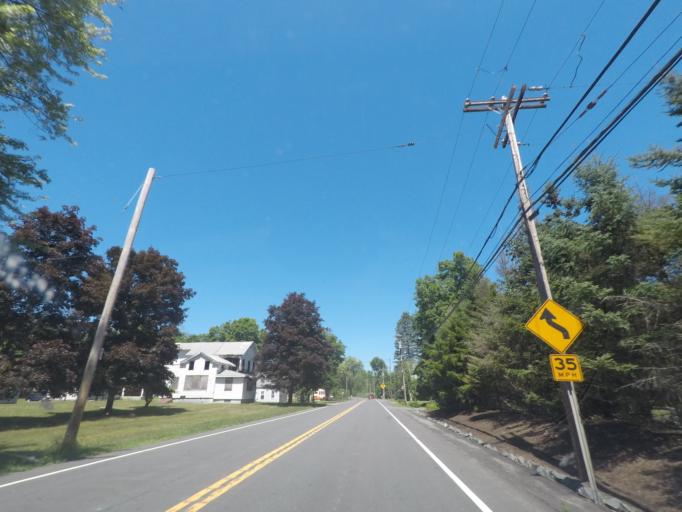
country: US
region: New York
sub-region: Rensselaer County
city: West Sand Lake
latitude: 42.6672
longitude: -73.6186
